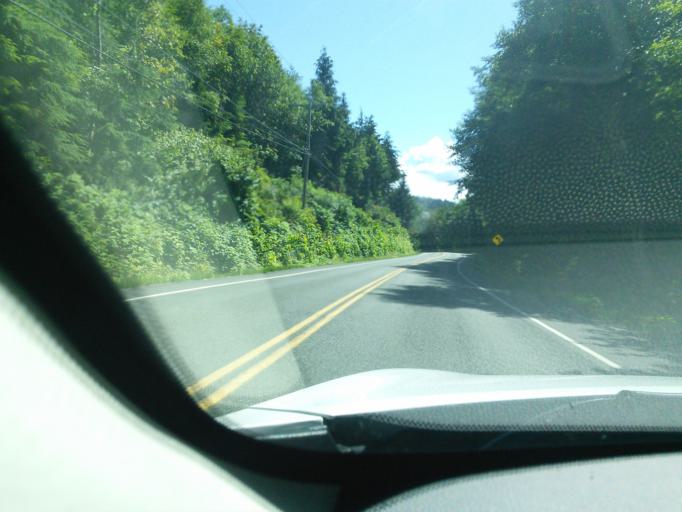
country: CA
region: British Columbia
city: Campbell River
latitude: 50.3459
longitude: -125.9064
